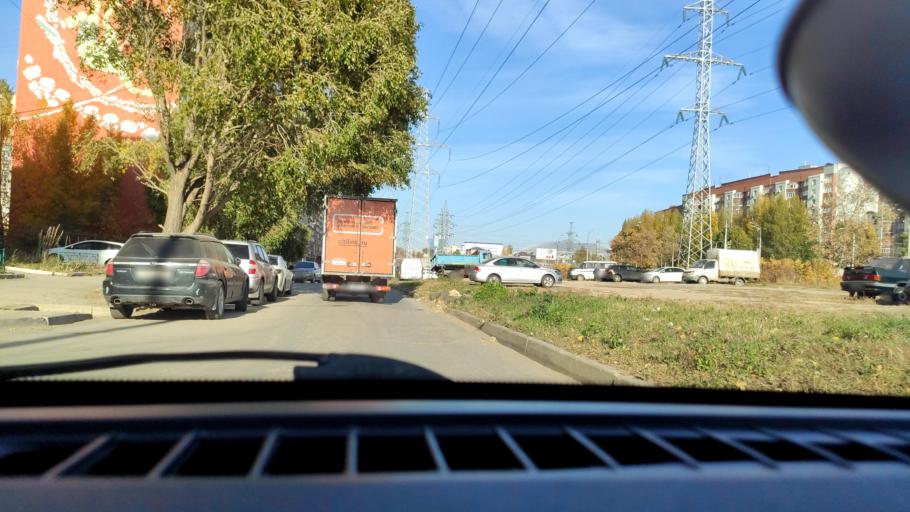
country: RU
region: Samara
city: Samara
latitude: 53.2656
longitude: 50.2181
